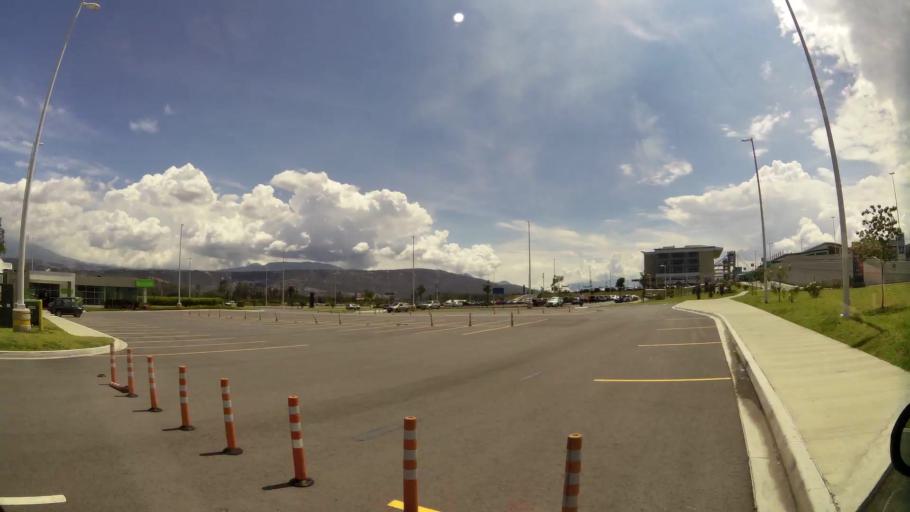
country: EC
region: Pichincha
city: Quito
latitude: -0.1271
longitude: -78.3611
